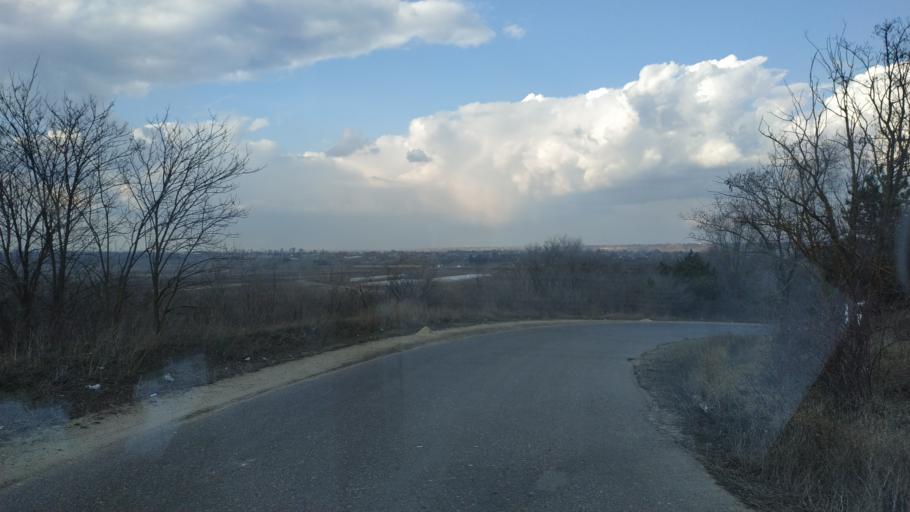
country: MD
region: Anenii Noi
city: Varnita
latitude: 46.9113
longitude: 29.4567
